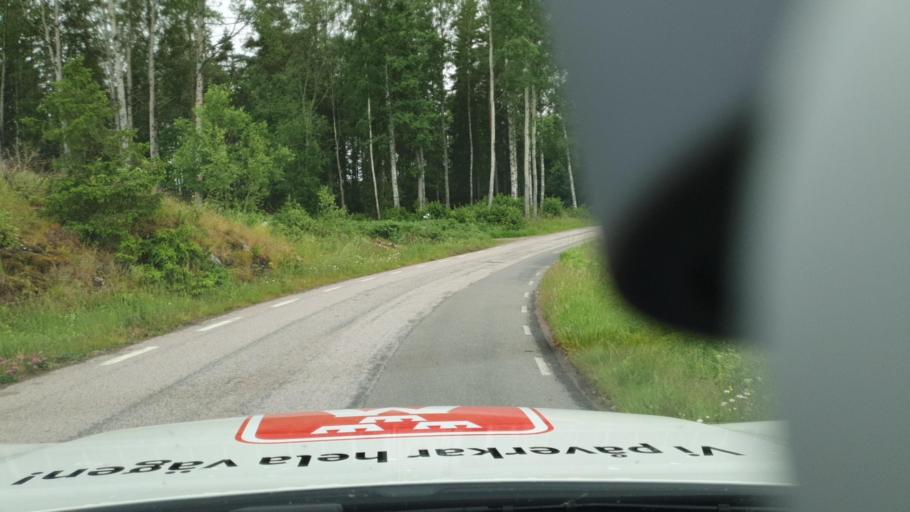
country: SE
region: Vaestra Goetaland
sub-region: Gullspangs Kommun
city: Gullspang
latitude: 59.0383
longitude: 14.1552
